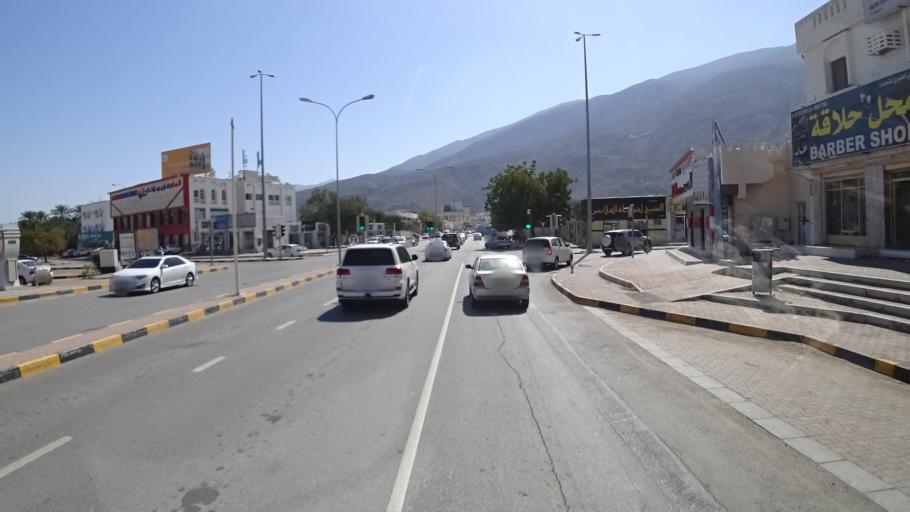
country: OM
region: Al Batinah
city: Rustaq
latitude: 23.3949
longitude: 57.4223
